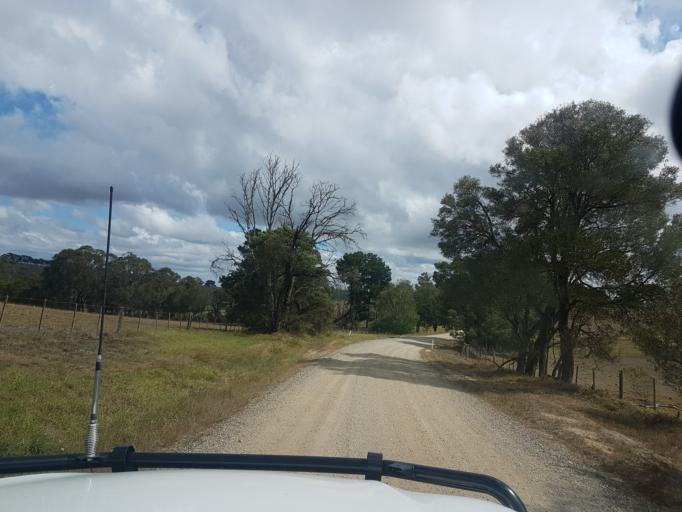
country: AU
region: Victoria
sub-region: East Gippsland
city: Bairnsdale
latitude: -37.7875
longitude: 147.5660
